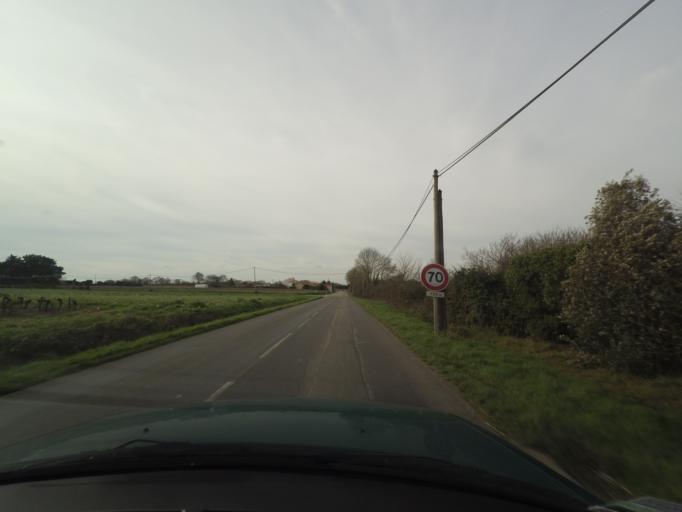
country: FR
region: Pays de la Loire
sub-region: Departement de la Loire-Atlantique
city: Saint-Lumine-de-Coutais
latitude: 47.0358
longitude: -1.6918
